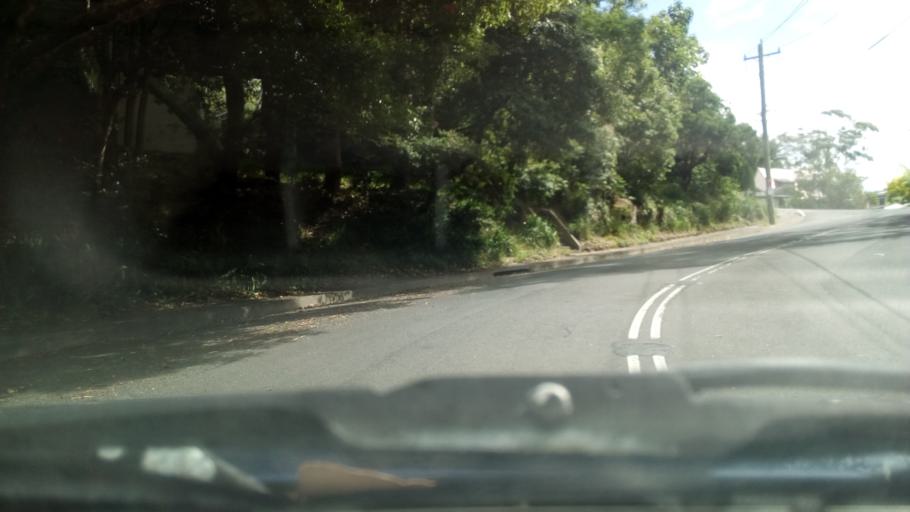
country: AU
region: New South Wales
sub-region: Wollongong
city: Mangerton
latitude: -34.4309
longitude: 150.8764
